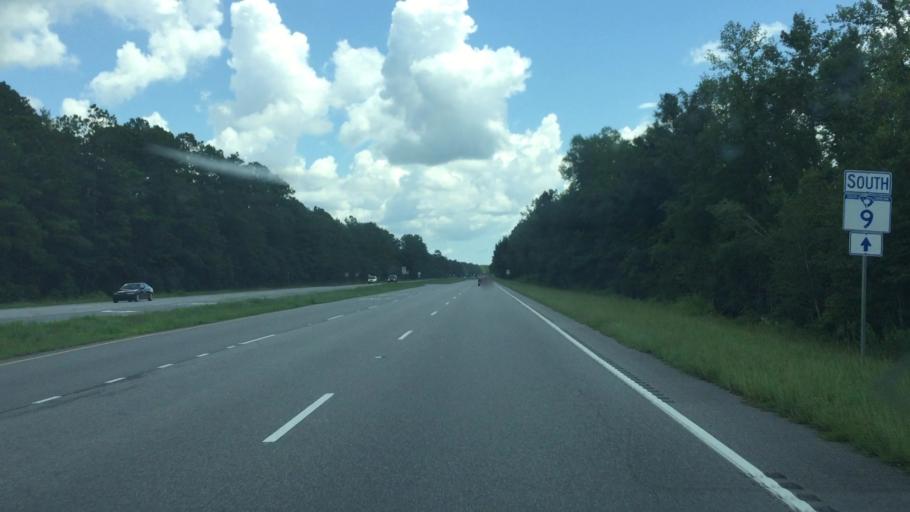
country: US
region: South Carolina
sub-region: Horry County
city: Loris
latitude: 34.0393
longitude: -78.8187
